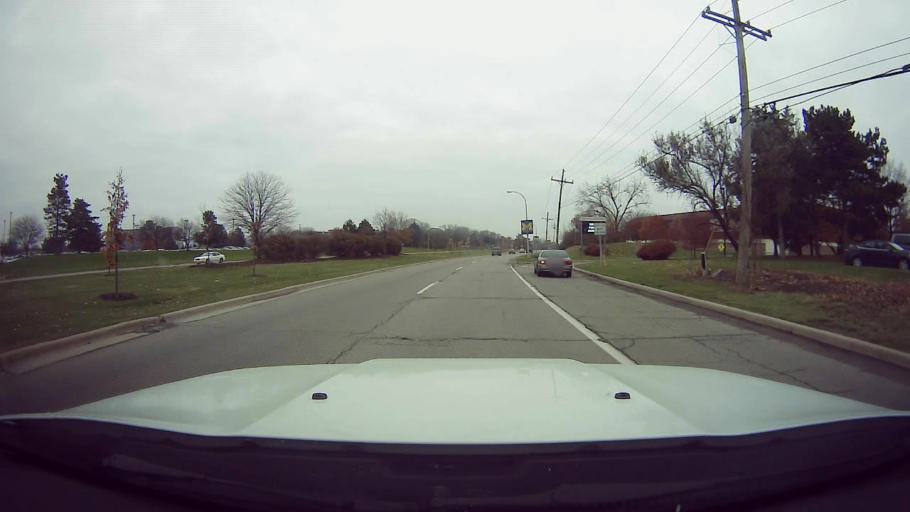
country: US
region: Michigan
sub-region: Wayne County
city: Dearborn Heights
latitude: 42.3158
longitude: -83.2279
